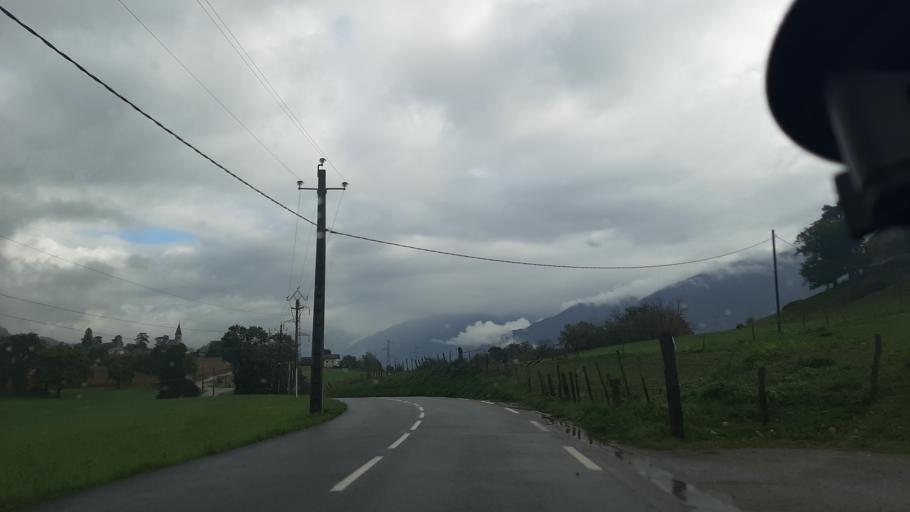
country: FR
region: Rhone-Alpes
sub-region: Departement de la Savoie
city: Gresy-sur-Isere
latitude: 45.6110
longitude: 6.2729
